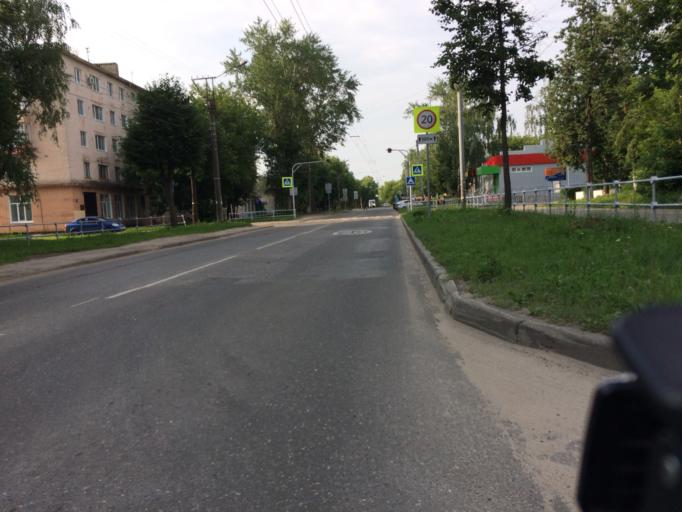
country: RU
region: Mariy-El
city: Yoshkar-Ola
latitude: 56.6241
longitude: 47.9461
